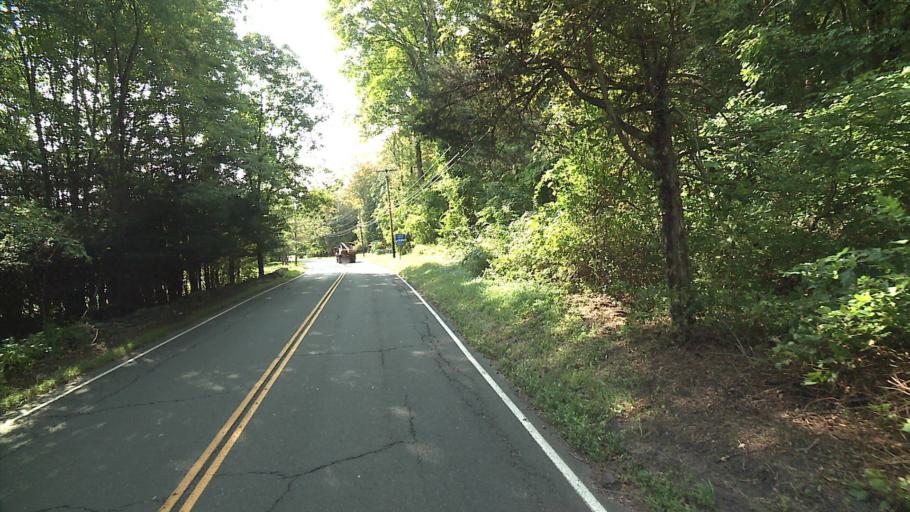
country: US
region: Connecticut
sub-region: Fairfield County
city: Georgetown
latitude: 41.2495
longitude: -73.3225
